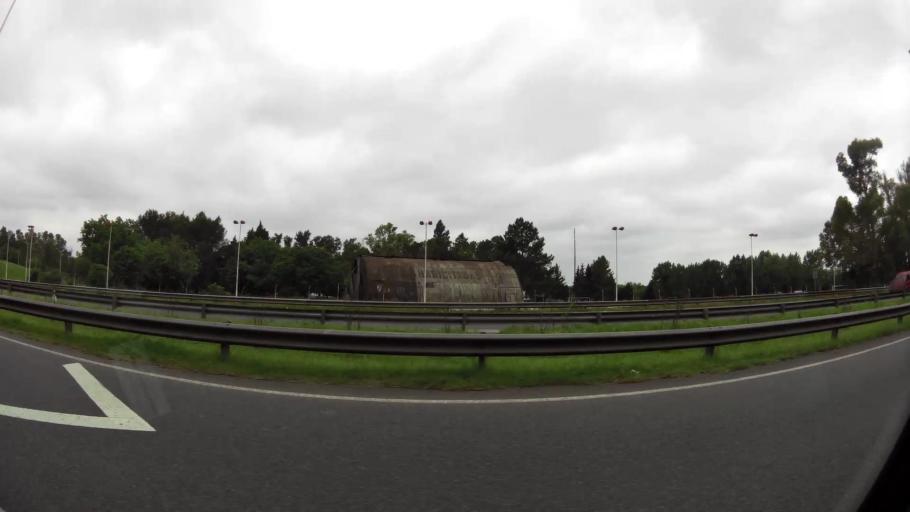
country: AR
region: Buenos Aires
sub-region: Partido de Ezeiza
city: Ezeiza
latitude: -34.8108
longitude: -58.5115
